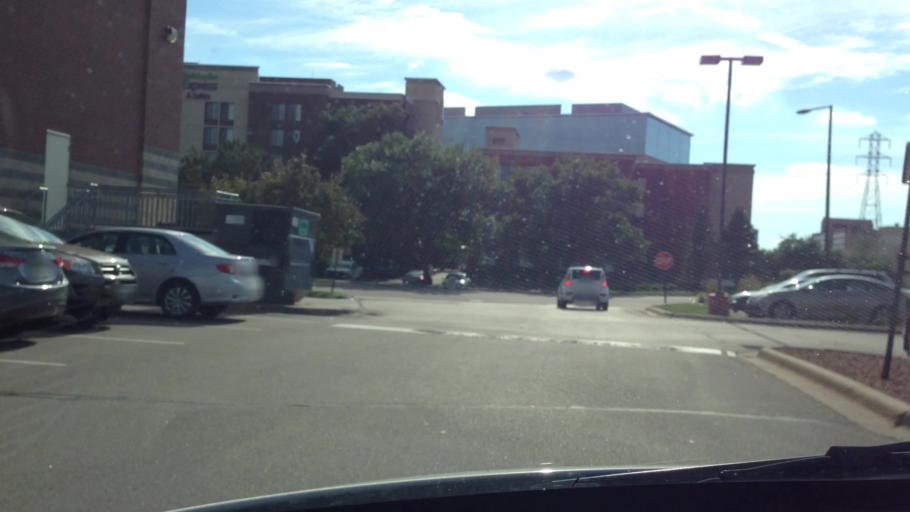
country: US
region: Minnesota
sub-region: Hennepin County
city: Edina
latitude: 44.8596
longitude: -93.3327
